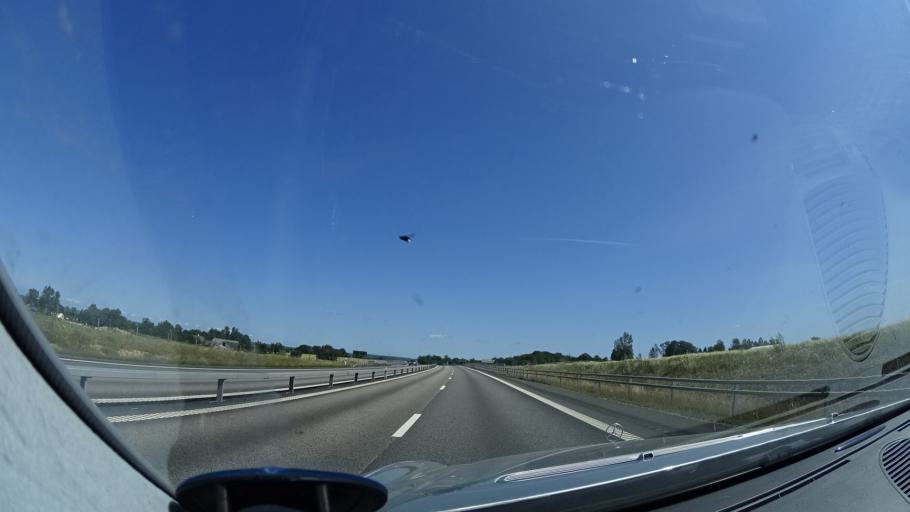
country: SE
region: Skane
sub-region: Hoors Kommun
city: Loberod
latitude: 55.8263
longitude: 13.5382
